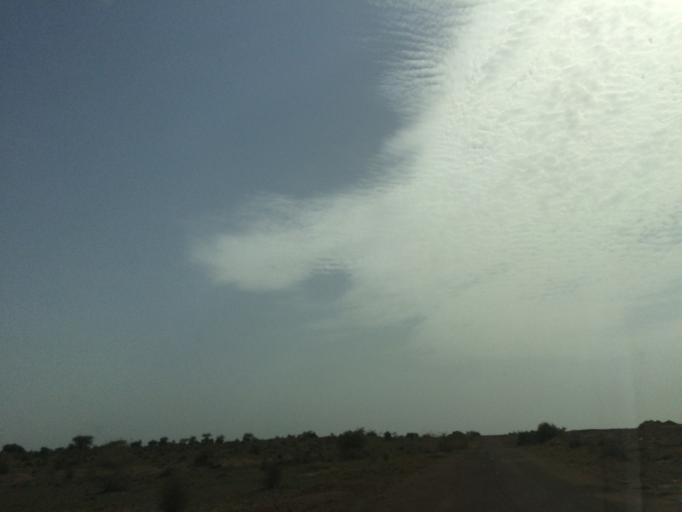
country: IN
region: Rajasthan
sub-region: Jaisalmer
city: Jaisalmer
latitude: 26.8673
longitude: 70.8656
